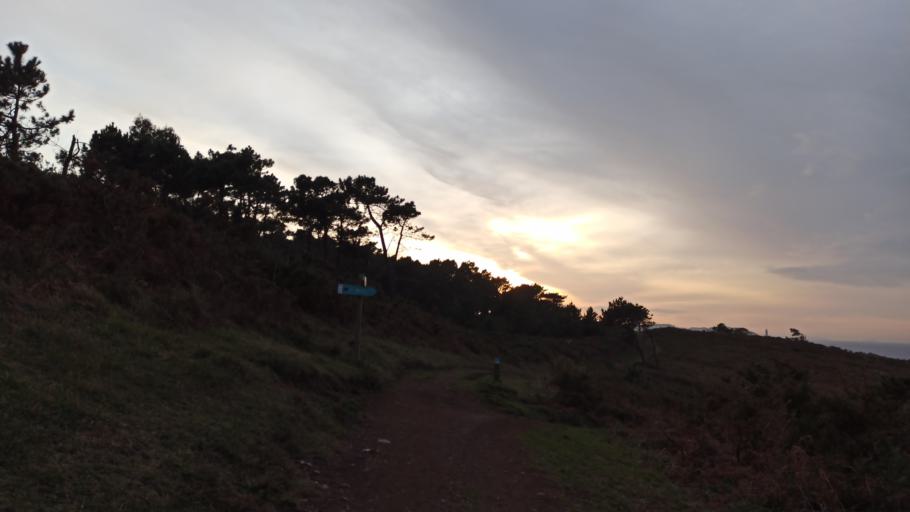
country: ES
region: Galicia
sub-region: Provincia da Coruna
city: A Coruna
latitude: 43.3969
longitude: -8.3381
